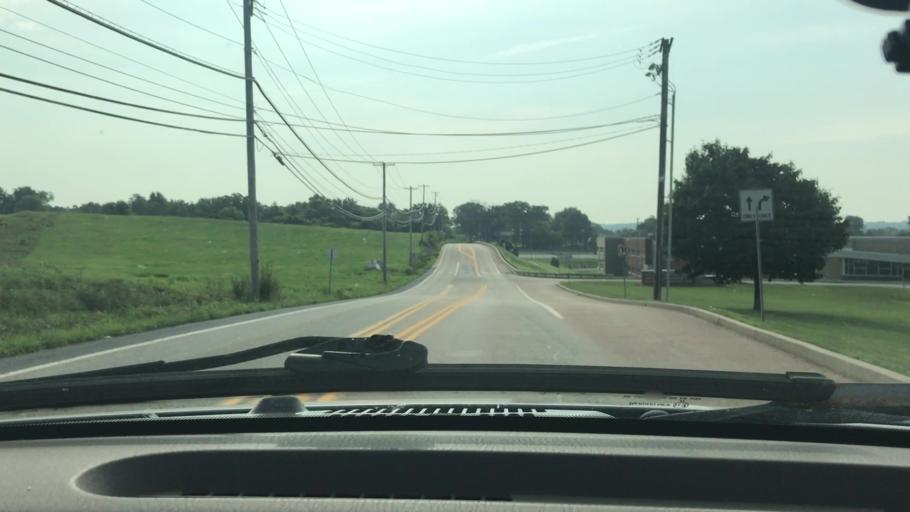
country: US
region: Pennsylvania
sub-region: Dauphin County
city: Middletown
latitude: 40.2142
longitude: -76.7403
